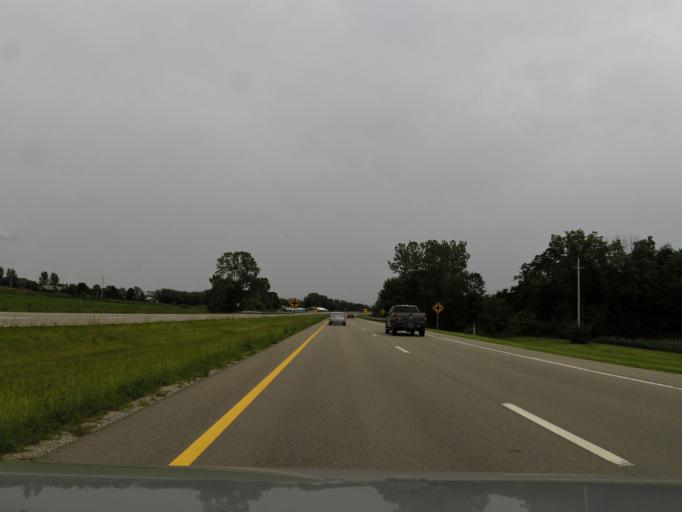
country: US
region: Ohio
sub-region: Warren County
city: Waynesville
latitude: 39.4989
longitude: -84.0046
